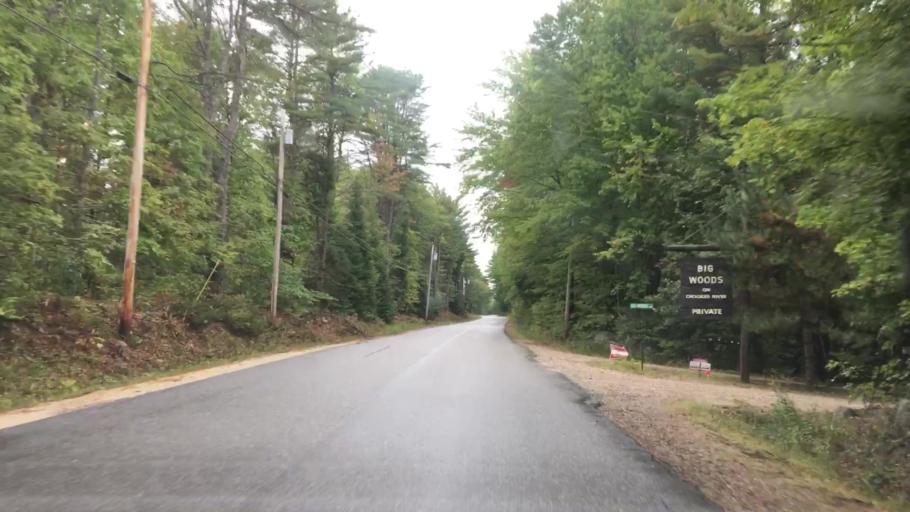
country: US
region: Maine
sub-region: Cumberland County
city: Harrison
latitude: 44.0407
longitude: -70.6097
